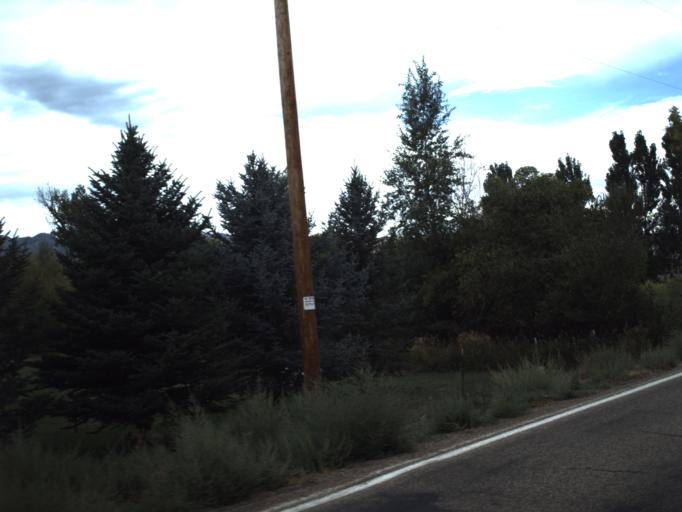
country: US
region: Utah
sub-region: Morgan County
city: Morgan
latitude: 40.9814
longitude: -111.6783
